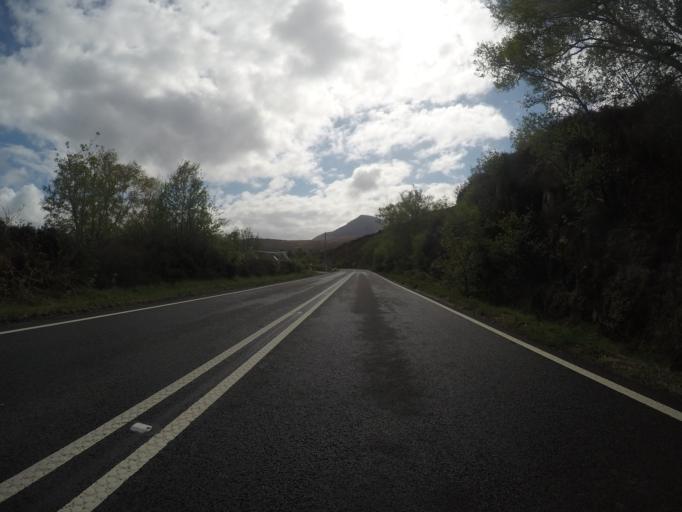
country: GB
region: Scotland
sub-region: Highland
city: Portree
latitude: 57.2739
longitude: -6.0003
